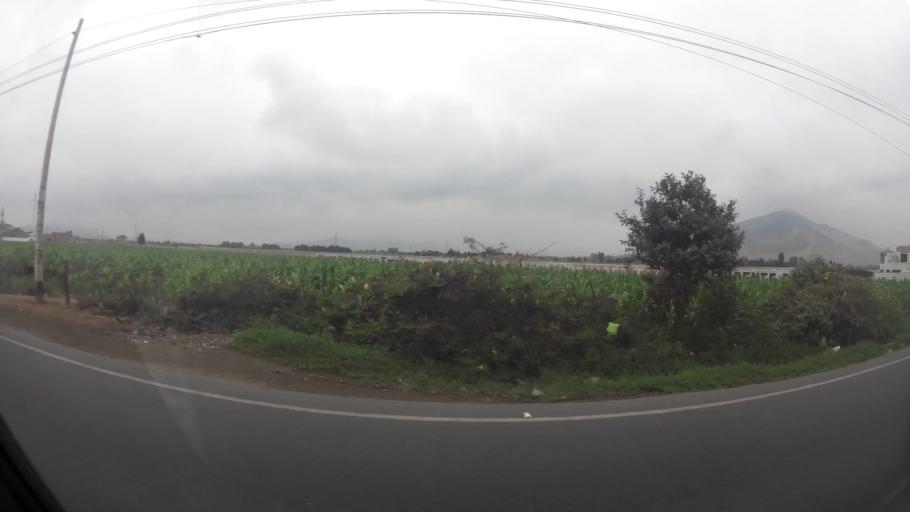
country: PE
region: Lima
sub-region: Provincia de Huaral
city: Huaral
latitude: -11.5077
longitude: -77.2313
